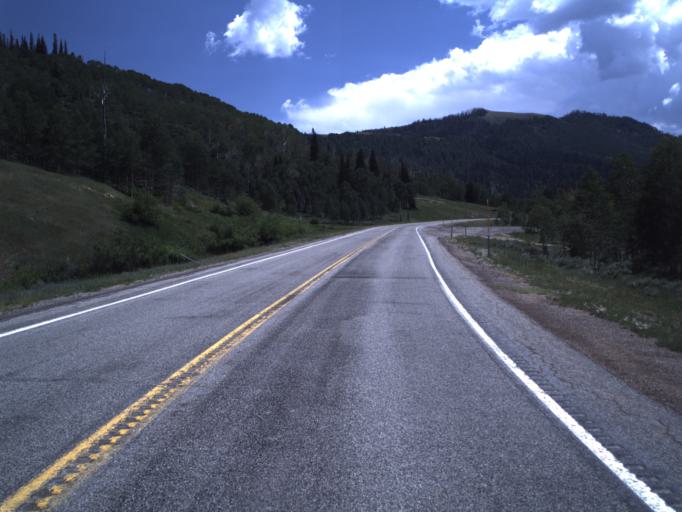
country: US
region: Utah
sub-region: Sanpete County
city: Fairview
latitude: 39.5872
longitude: -111.2409
